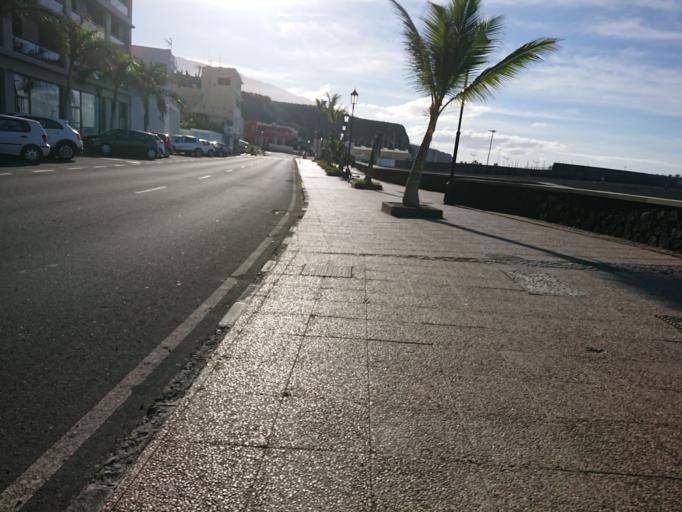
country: ES
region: Canary Islands
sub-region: Provincia de Santa Cruz de Tenerife
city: Tazacorte
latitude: 28.6488
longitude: -17.9449
